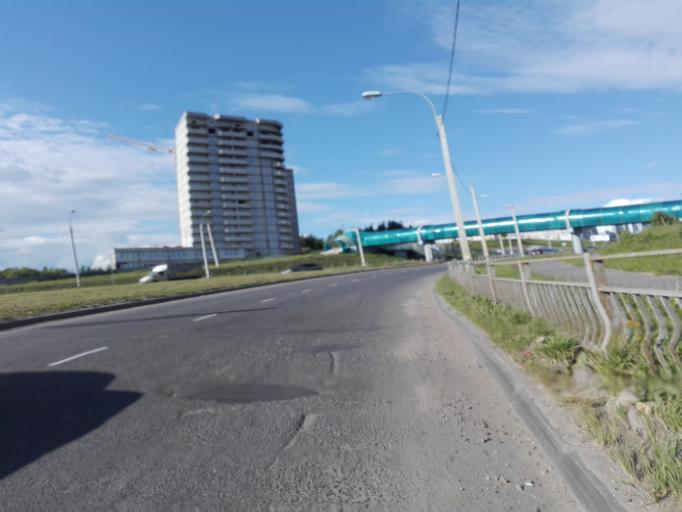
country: RU
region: Orjol
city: Orel
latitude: 53.0006
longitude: 36.1043
